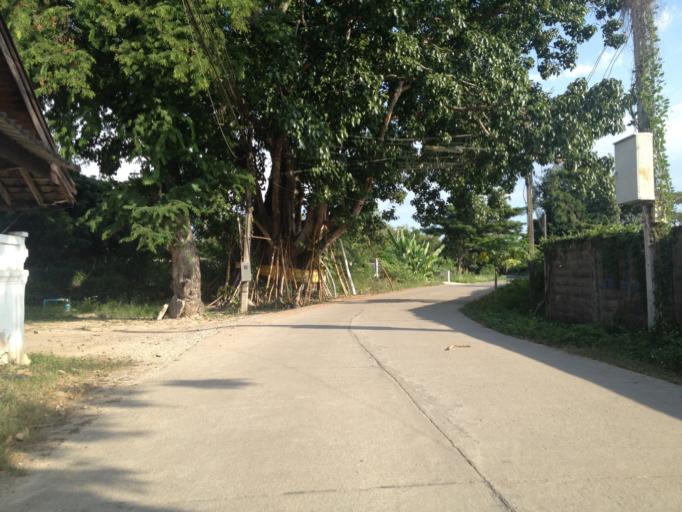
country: TH
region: Chiang Mai
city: Hang Dong
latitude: 18.6929
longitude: 98.9518
